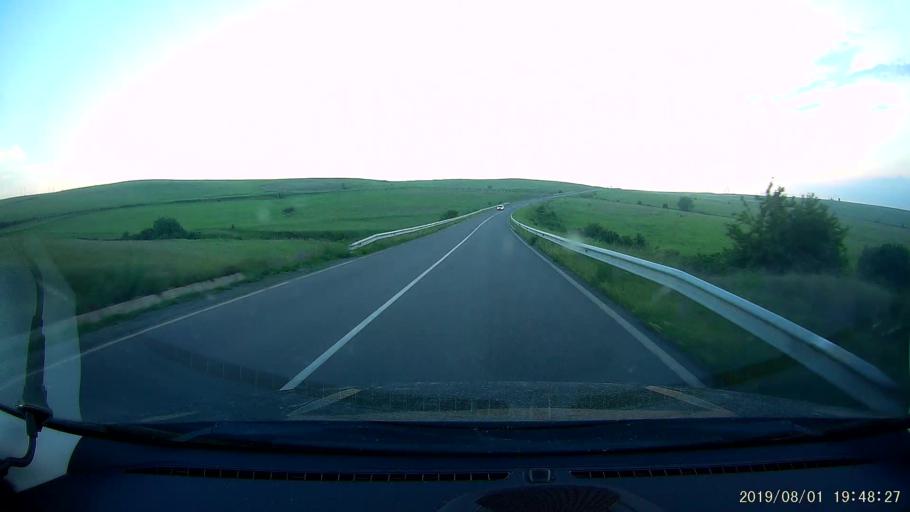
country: BG
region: Burgas
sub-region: Obshtina Karnobat
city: Karnobat
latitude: 42.6365
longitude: 26.9494
